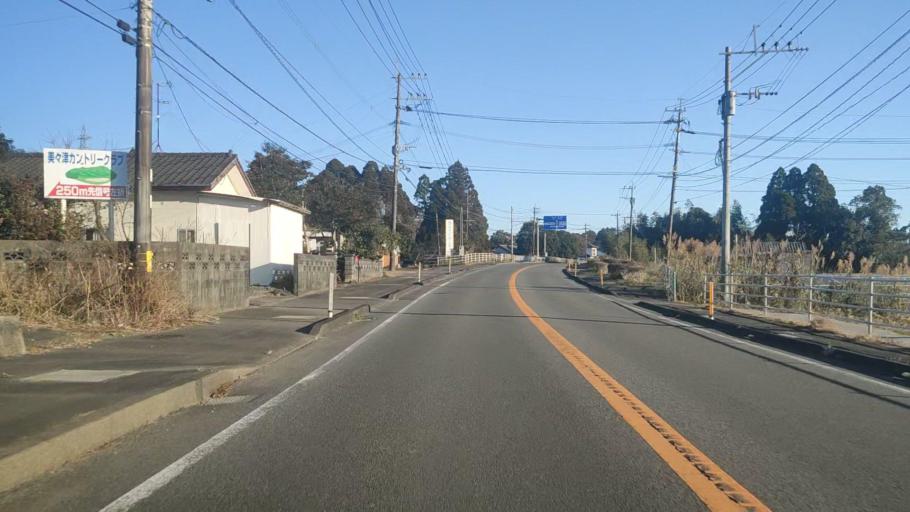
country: JP
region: Miyazaki
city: Takanabe
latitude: 32.3091
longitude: 131.5845
